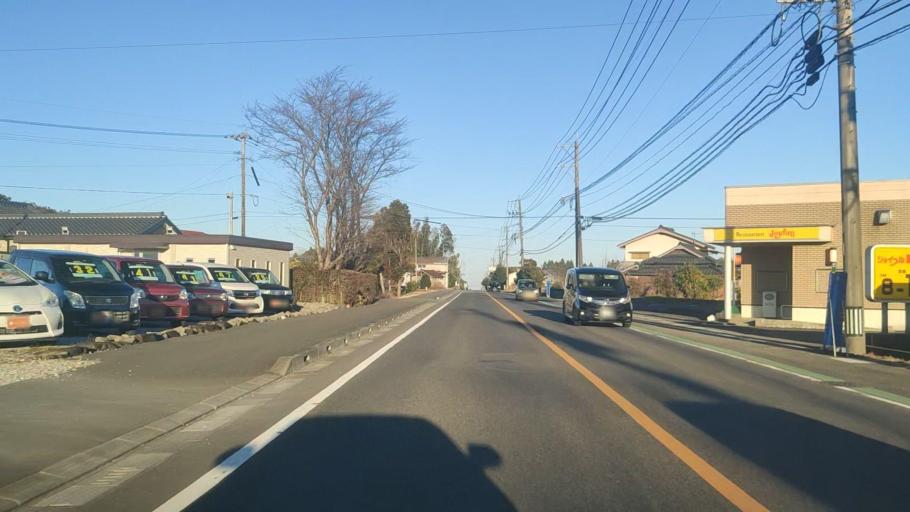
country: JP
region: Miyazaki
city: Miyazaki-shi
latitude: 31.8338
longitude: 131.3213
